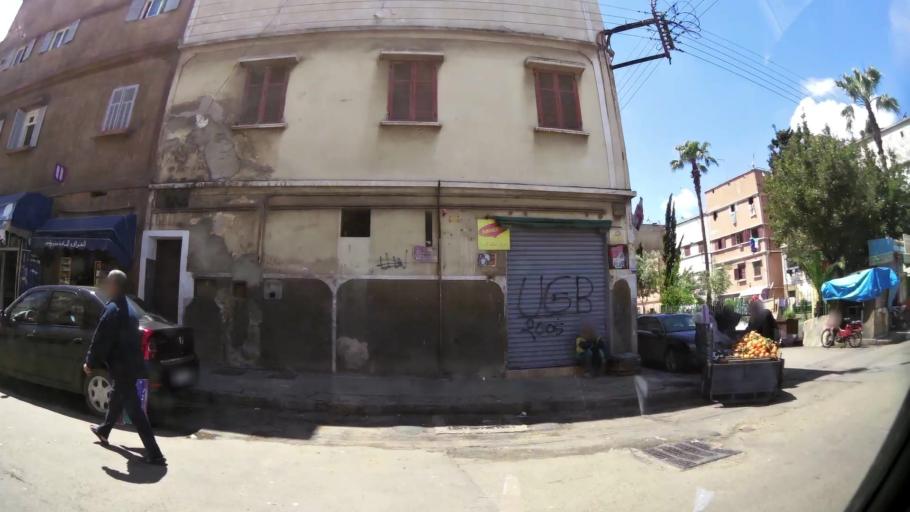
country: MA
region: Grand Casablanca
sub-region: Casablanca
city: Casablanca
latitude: 33.5635
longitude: -7.5735
